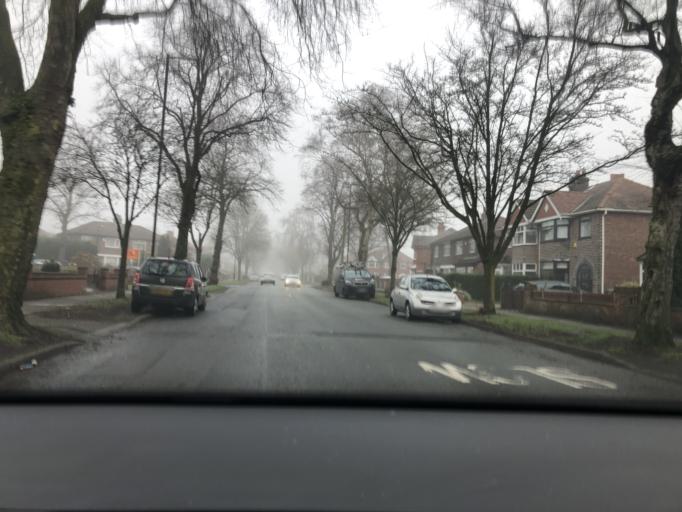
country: GB
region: England
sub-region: Trafford
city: Urmston
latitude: 53.4526
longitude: -2.3623
